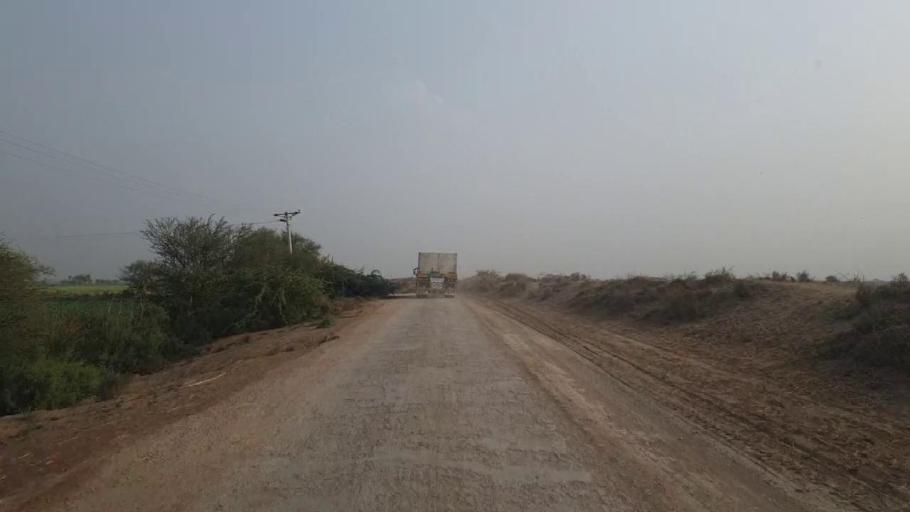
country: PK
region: Sindh
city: Mirpur Batoro
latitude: 24.5678
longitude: 68.3994
